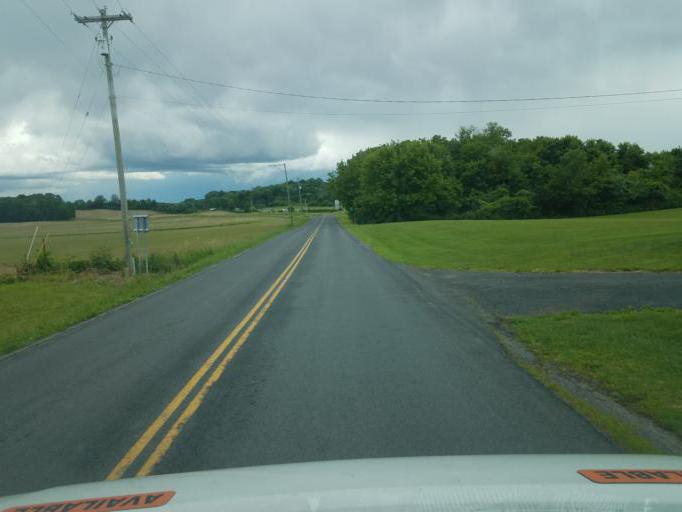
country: US
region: New York
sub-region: Ontario County
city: Geneva
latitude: 42.9576
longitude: -76.9635
